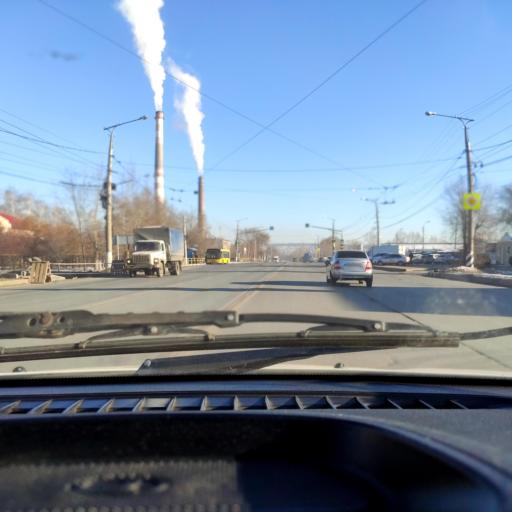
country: RU
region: Samara
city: Zhigulevsk
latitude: 53.4870
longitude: 49.4876
